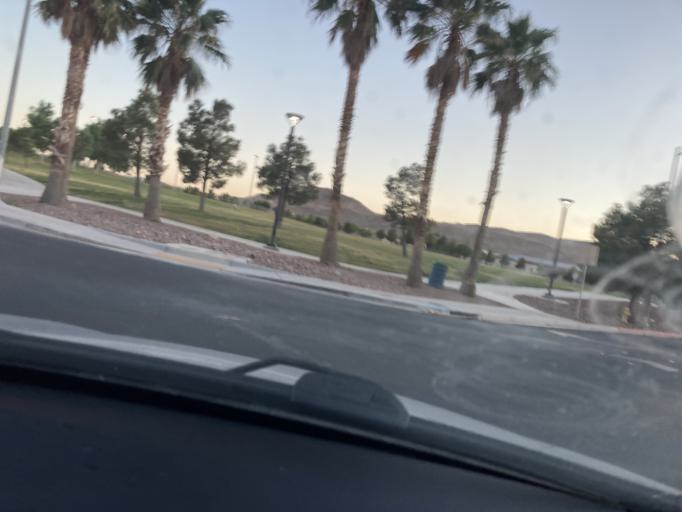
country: US
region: Nevada
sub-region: Clark County
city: Enterprise
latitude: 36.0629
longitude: -115.2884
